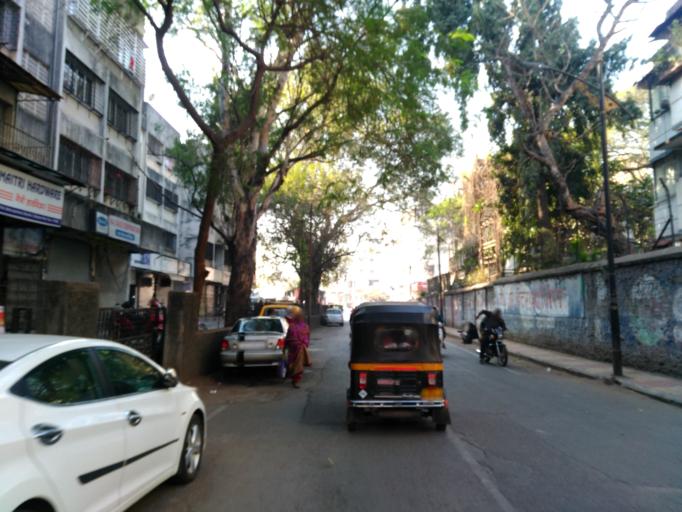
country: IN
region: Maharashtra
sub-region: Pune Division
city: Pune
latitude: 18.5101
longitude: 73.8724
